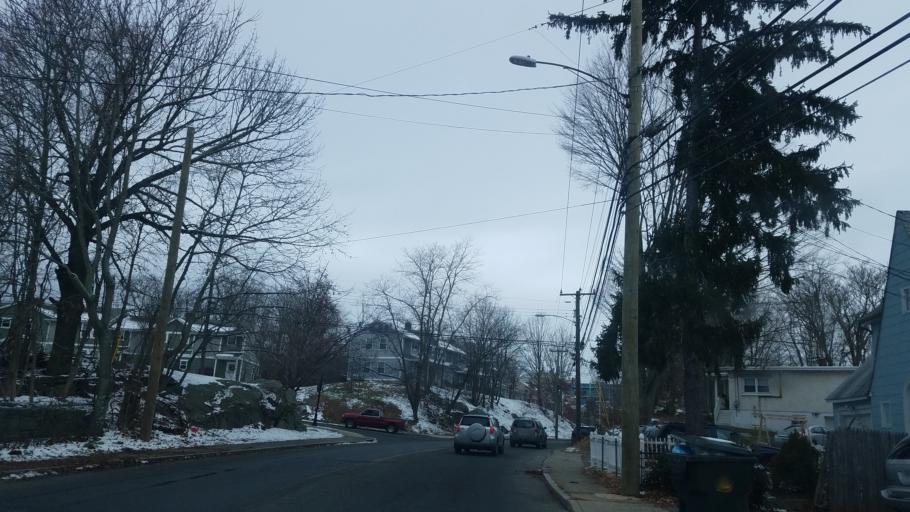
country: US
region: Connecticut
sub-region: New London County
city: Central Waterford
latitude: 41.3574
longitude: -72.1170
